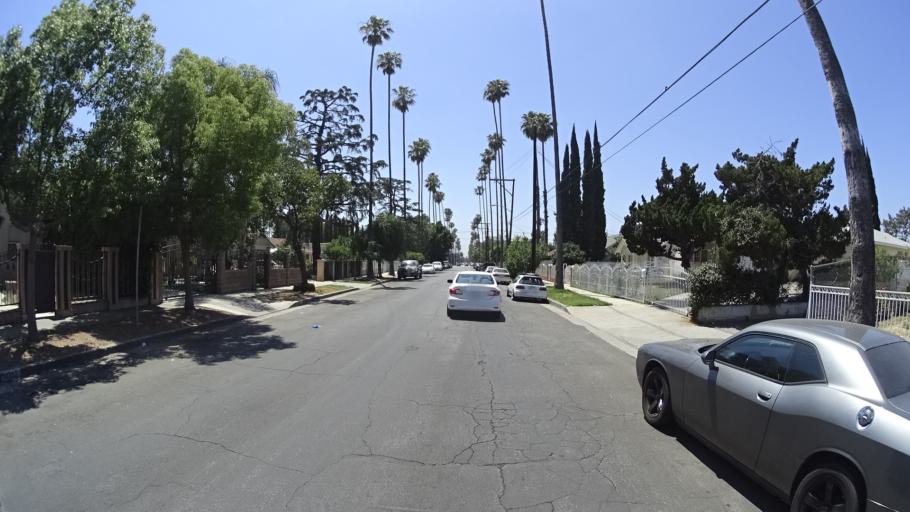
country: US
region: California
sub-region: Los Angeles County
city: Van Nuys
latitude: 34.1907
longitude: -118.4448
